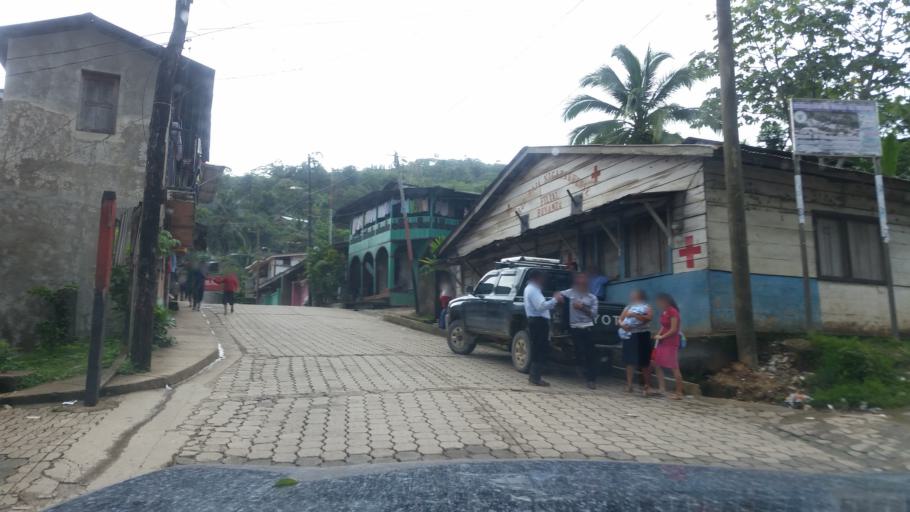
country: NI
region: Atlantico Norte (RAAN)
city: Bonanza
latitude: 14.0305
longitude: -84.5988
